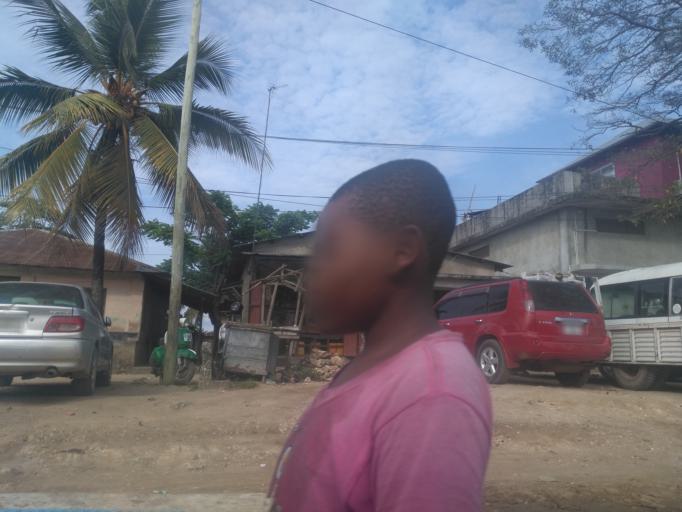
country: TZ
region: Zanzibar Urban/West
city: Zanzibar
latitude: -6.1610
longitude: 39.2096
